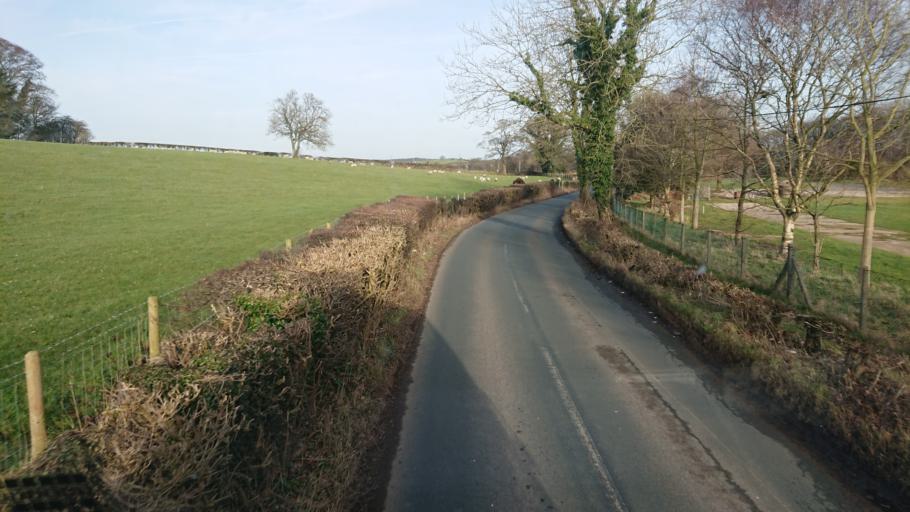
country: GB
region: England
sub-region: Lancashire
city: Bolton le Sands
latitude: 54.0737
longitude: -2.7798
